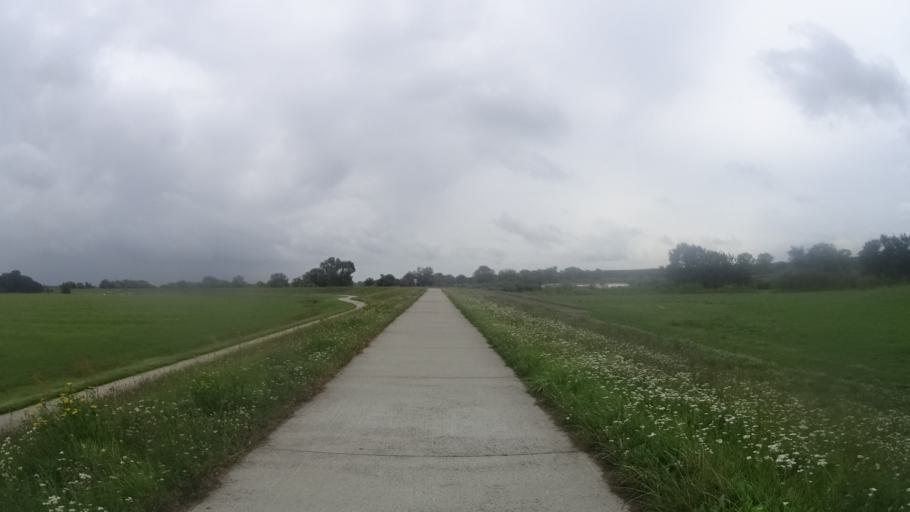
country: DE
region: Lower Saxony
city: Bleckede
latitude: 53.2964
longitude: 10.7626
